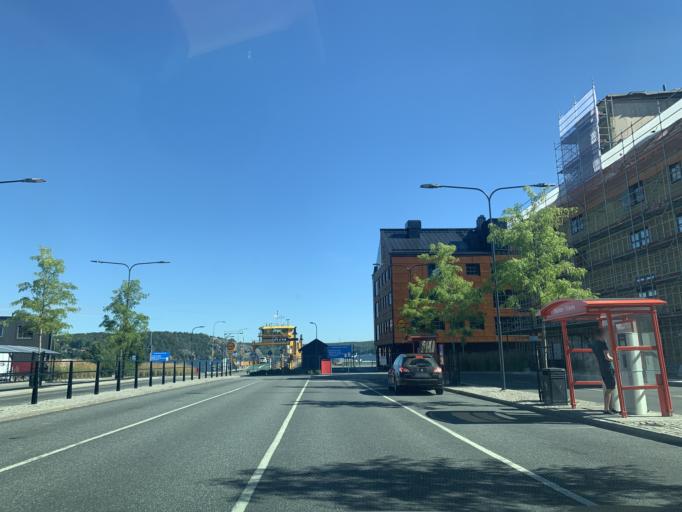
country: SE
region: Stockholm
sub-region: Botkyrka Kommun
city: Fittja
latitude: 59.2717
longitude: 17.8445
